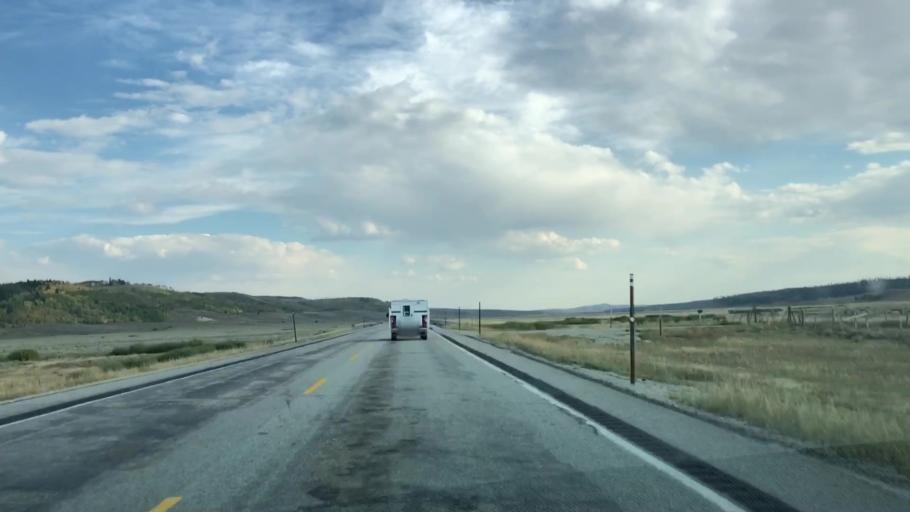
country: US
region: Wyoming
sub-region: Sublette County
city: Pinedale
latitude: 43.1127
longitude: -110.1745
